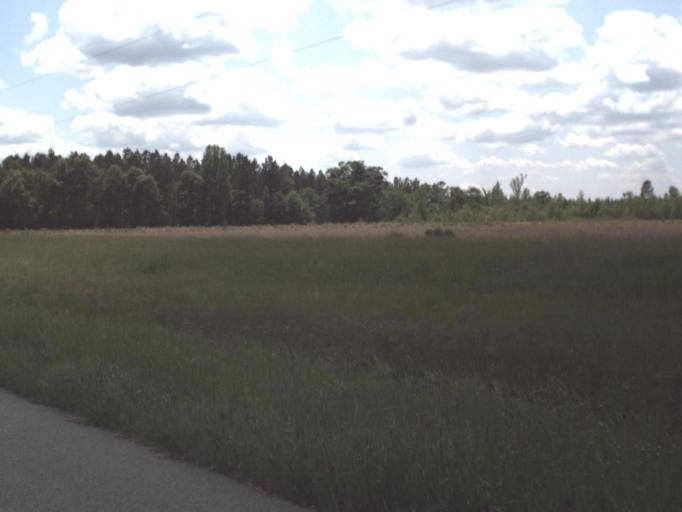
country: US
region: Florida
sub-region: Escambia County
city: Molino
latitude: 30.8302
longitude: -87.4354
